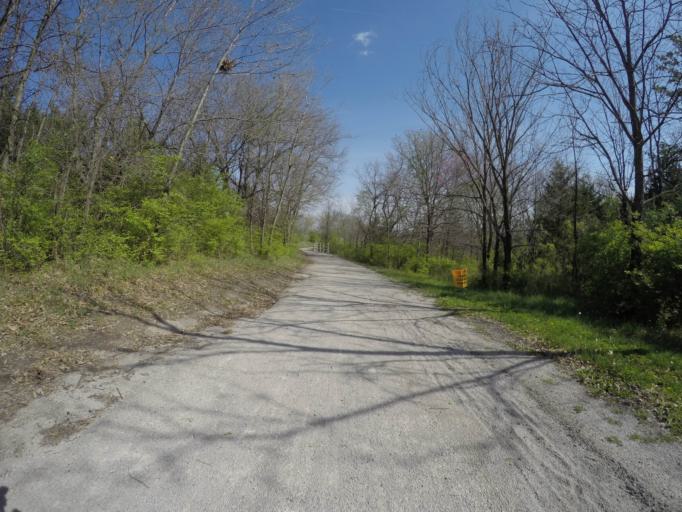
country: US
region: Missouri
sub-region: Jackson County
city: Grandview
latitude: 38.8961
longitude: -94.4924
